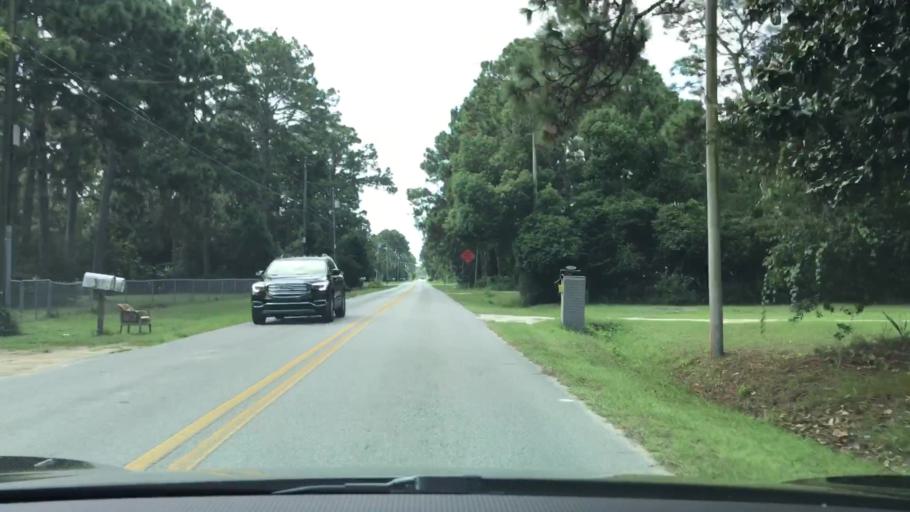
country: US
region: Florida
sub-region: Bay County
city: Panama City Beach
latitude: 30.1801
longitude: -85.7866
